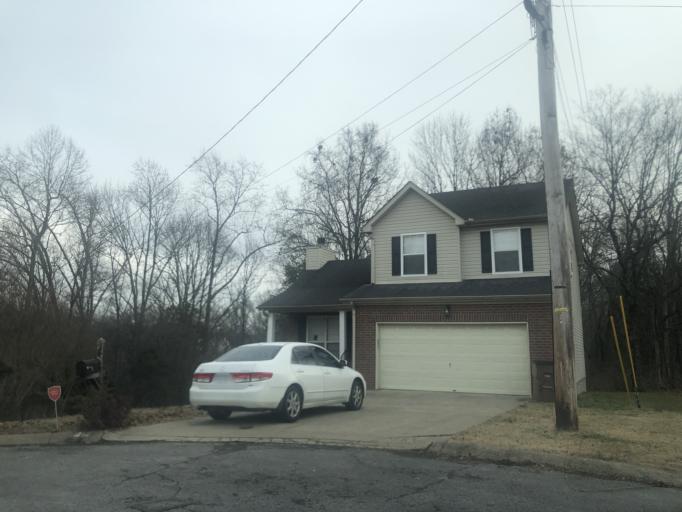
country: US
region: Tennessee
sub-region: Rutherford County
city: La Vergne
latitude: 36.0726
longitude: -86.6519
